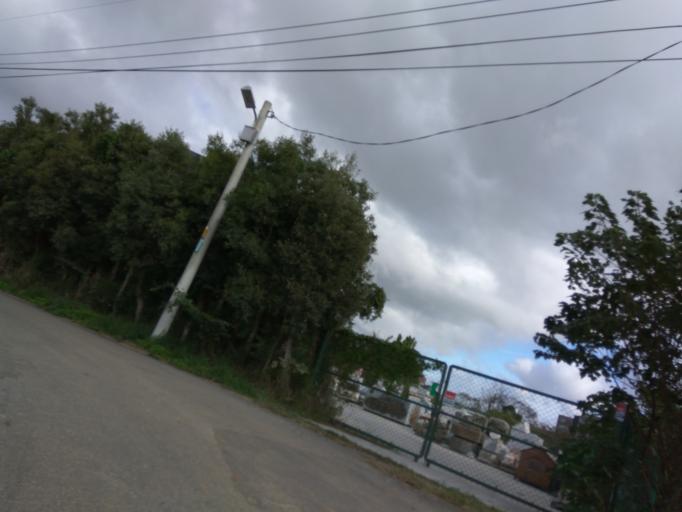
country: TW
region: Taiwan
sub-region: Hsinchu
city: Zhubei
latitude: 24.9684
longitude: 121.0852
